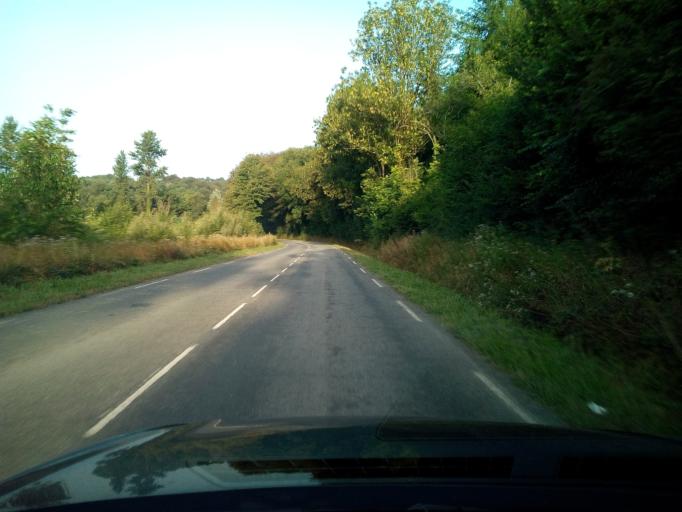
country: FR
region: Brittany
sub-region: Departement du Finistere
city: La Roche-Maurice
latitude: 48.4866
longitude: -4.1723
